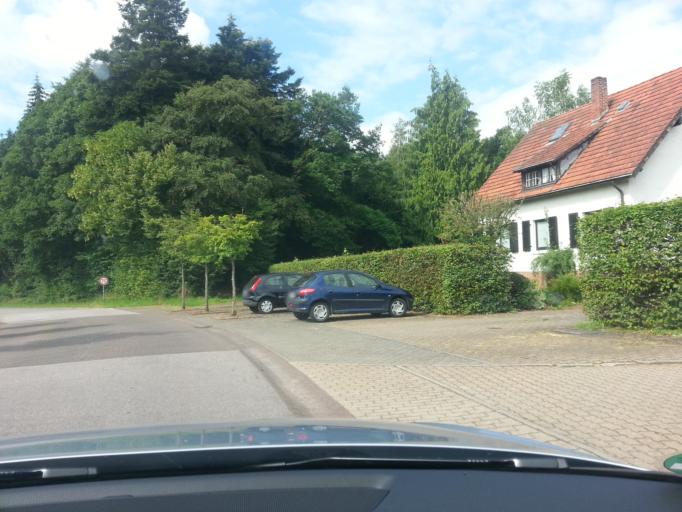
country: DE
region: Saarland
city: Weiten
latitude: 49.5269
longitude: 6.5257
